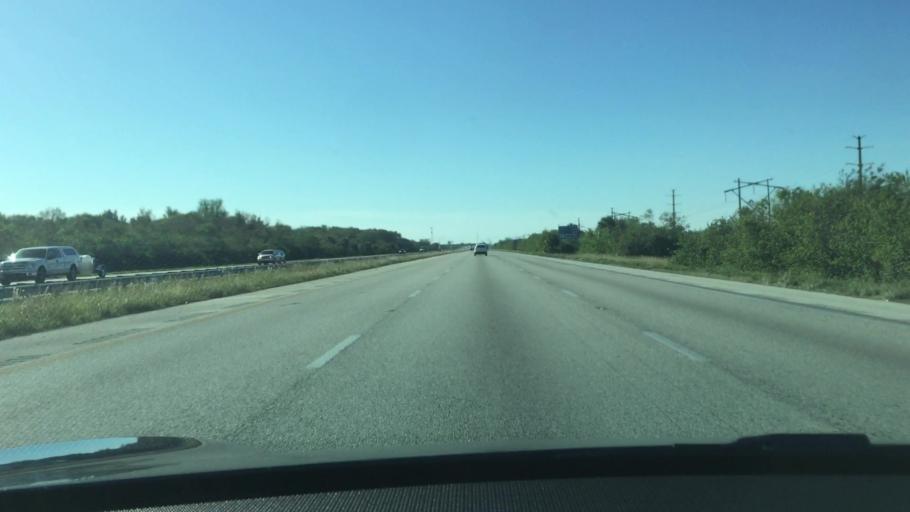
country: US
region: Florida
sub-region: Brevard County
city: June Park
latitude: 28.0984
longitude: -80.7061
